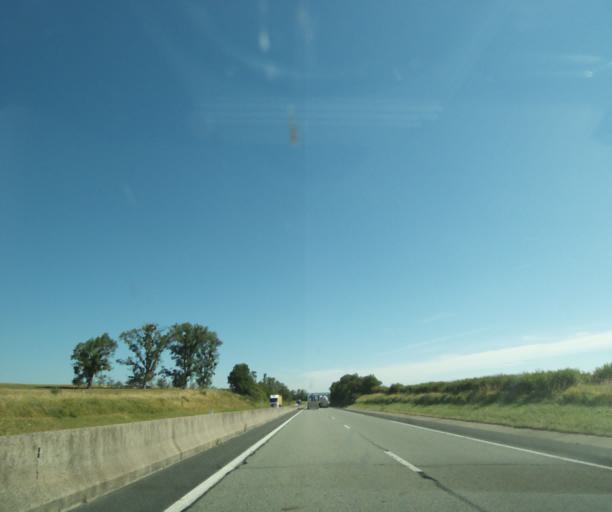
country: FR
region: Lorraine
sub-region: Departement des Vosges
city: Lamarche
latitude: 48.1204
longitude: 5.6630
